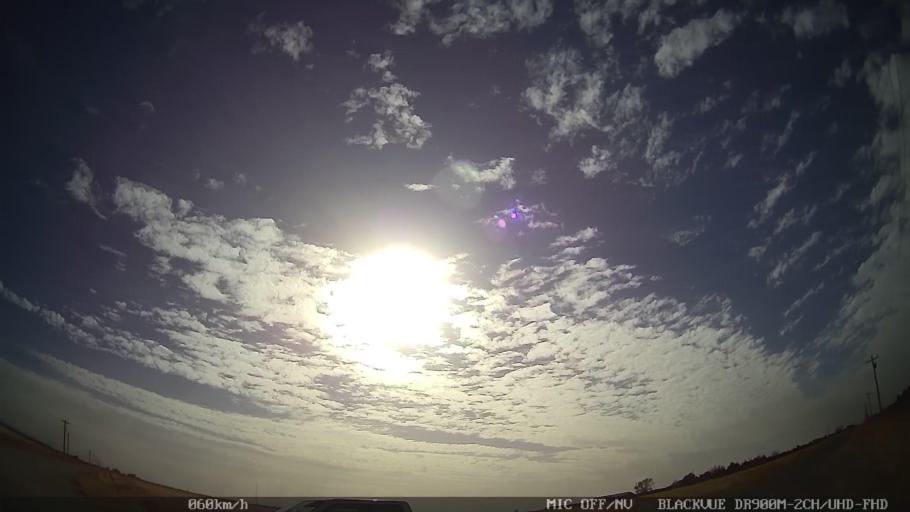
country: US
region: New Mexico
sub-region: Curry County
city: Texico
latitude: 34.4194
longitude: -103.0901
